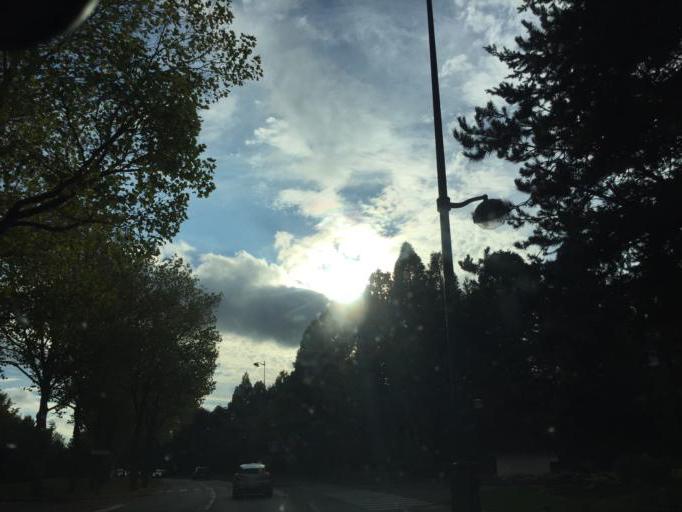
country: FR
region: Ile-de-France
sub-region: Departement de Seine-et-Marne
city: Magny-le-Hongre
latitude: 48.8691
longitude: 2.7929
